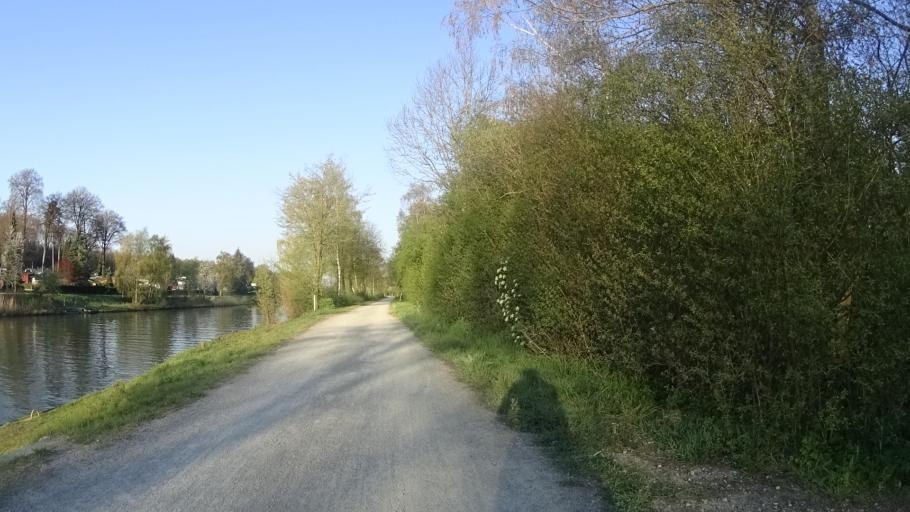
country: DE
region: North Rhine-Westphalia
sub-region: Regierungsbezirk Dusseldorf
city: Schermbeck
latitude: 51.6723
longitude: 6.8473
